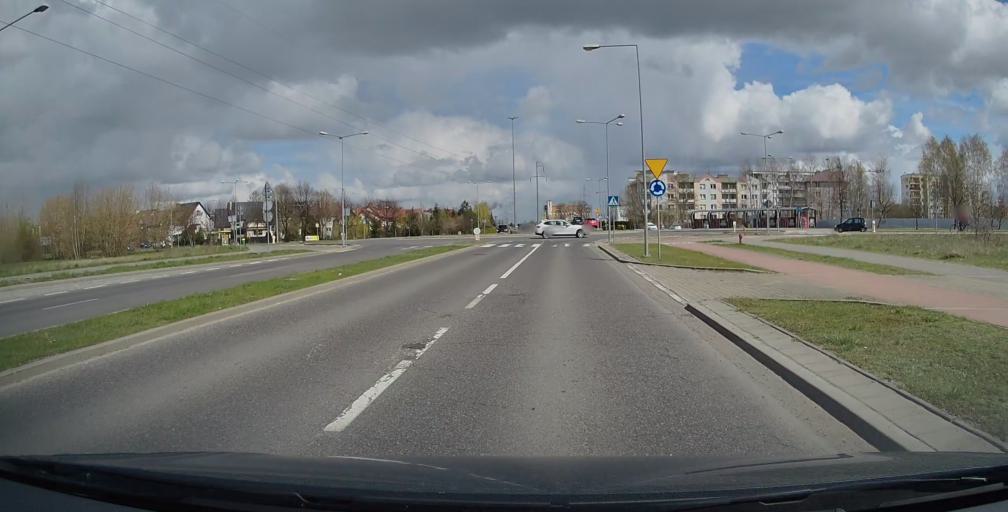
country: PL
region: Masovian Voivodeship
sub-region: Ostroleka
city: Ostroleka
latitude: 53.0673
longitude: 21.5900
